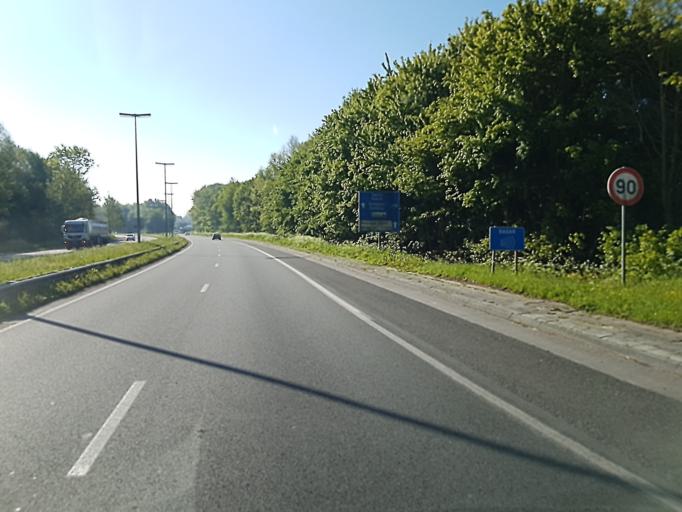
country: BE
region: Wallonia
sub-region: Province du Hainaut
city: Mouscron
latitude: 50.7537
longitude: 3.2061
